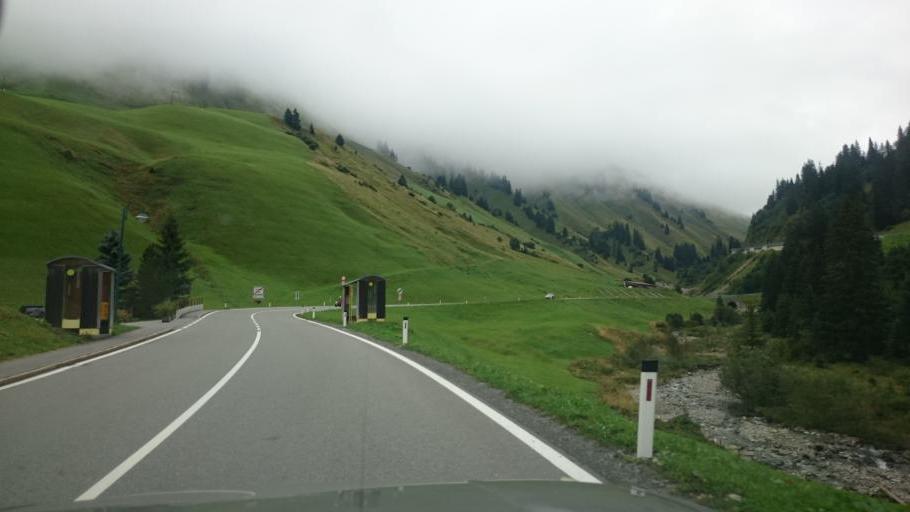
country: AT
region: Vorarlberg
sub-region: Politischer Bezirk Bregenz
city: Schroecken
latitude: 47.2629
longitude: 10.1049
